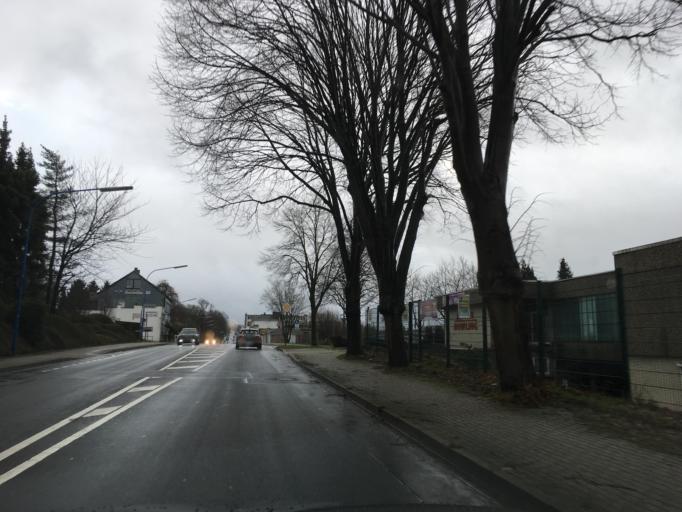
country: DE
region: North Rhine-Westphalia
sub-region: Regierungsbezirk Dusseldorf
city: Velbert
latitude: 51.3258
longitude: 7.0580
